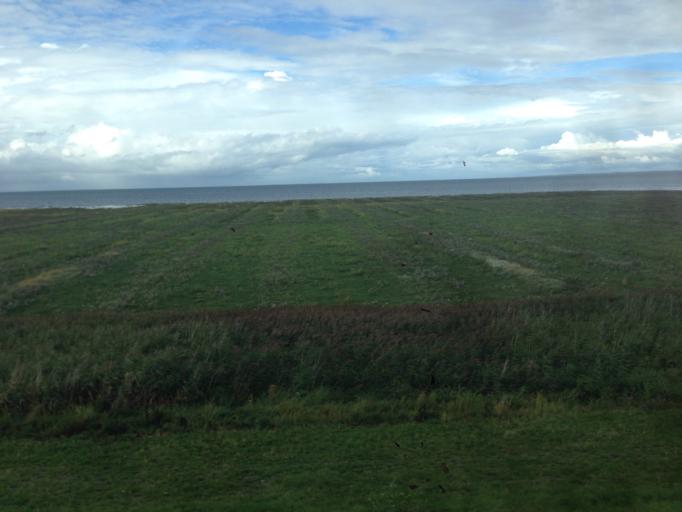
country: DE
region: Schleswig-Holstein
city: Friedrich-Wilhelm-Lubke-Koog
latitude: 54.8855
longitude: 8.5780
